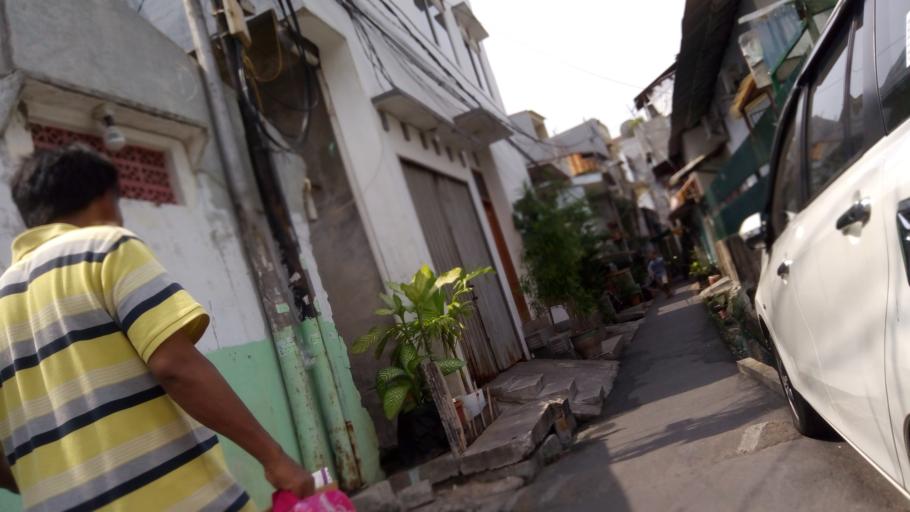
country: ID
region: Jakarta Raya
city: Jakarta
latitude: -6.1498
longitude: 106.8303
